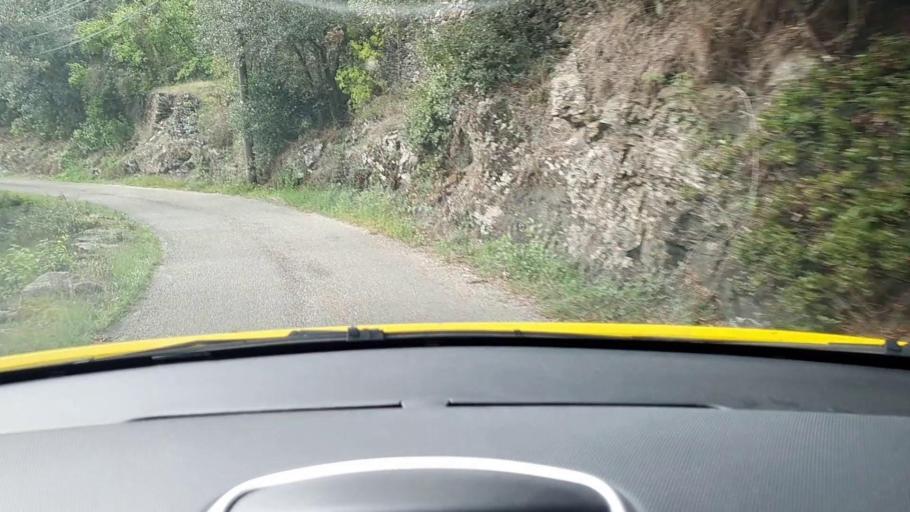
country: FR
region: Languedoc-Roussillon
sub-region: Departement du Gard
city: Sumene
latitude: 44.0075
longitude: 3.6595
